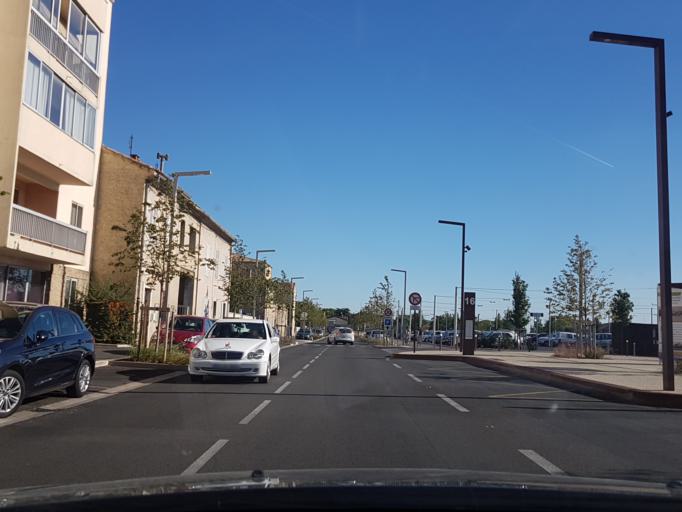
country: FR
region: Provence-Alpes-Cote d'Azur
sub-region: Departement du Vaucluse
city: Carpentras
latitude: 44.0475
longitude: 5.0456
